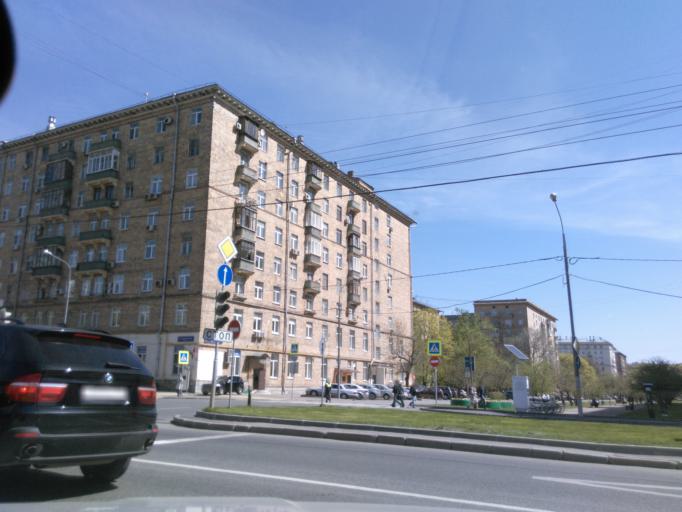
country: RU
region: Moscow
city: Luzhniki
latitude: 55.7222
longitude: 37.5754
